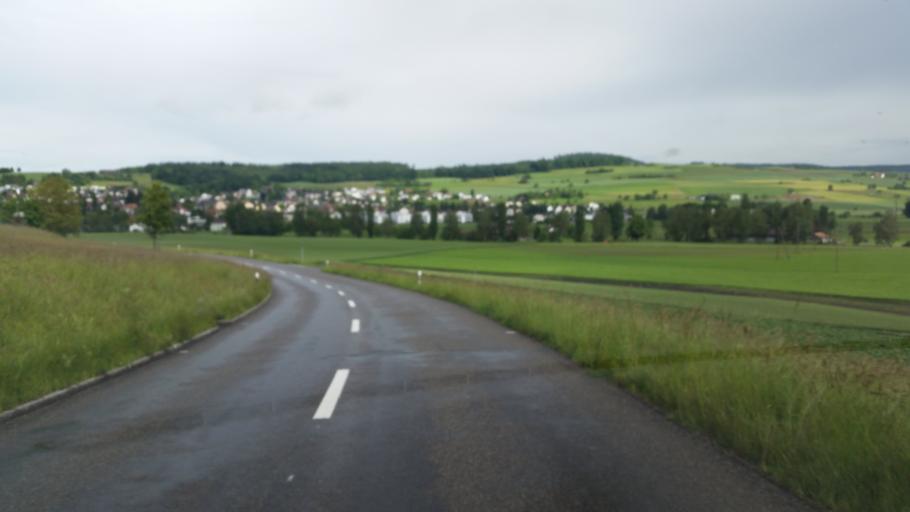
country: CH
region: Aargau
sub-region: Bezirk Bremgarten
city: Sarmenstorf
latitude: 47.3122
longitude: 8.2337
